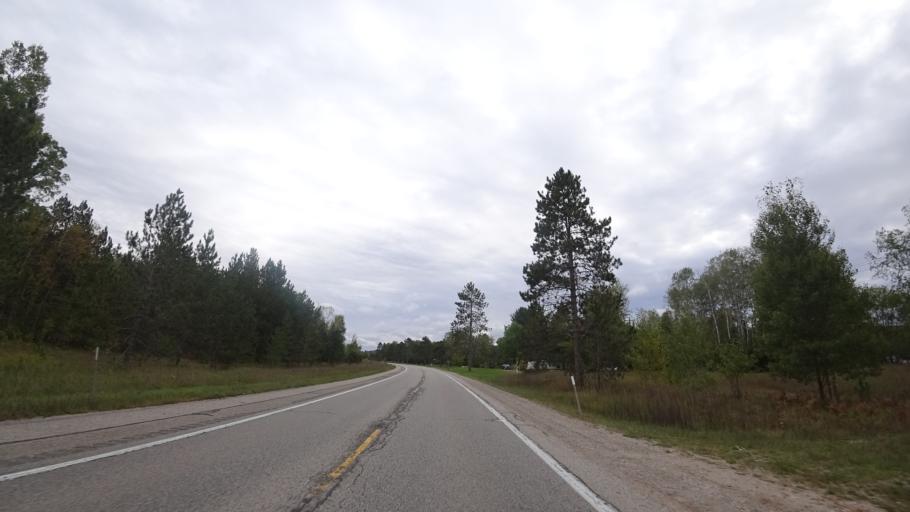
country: US
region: Michigan
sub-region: Charlevoix County
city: Boyne City
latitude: 45.2152
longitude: -84.9251
